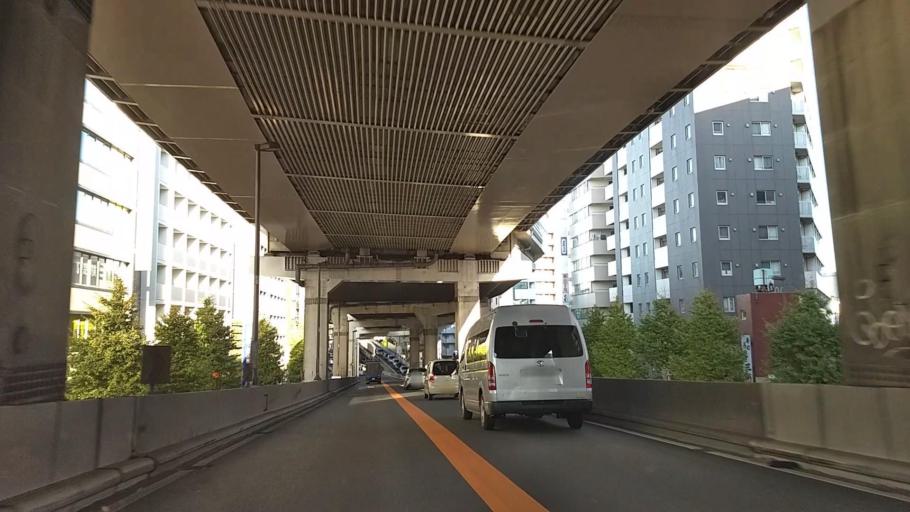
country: JP
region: Tokyo
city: Tokyo
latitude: 35.6436
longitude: 139.6711
